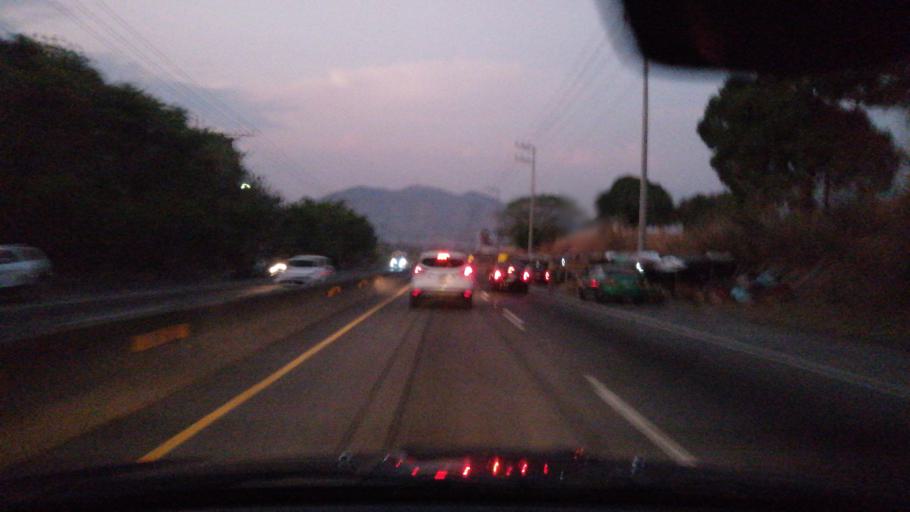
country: SV
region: San Salvador
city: Ayutuxtepeque
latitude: 13.7629
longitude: -89.2130
